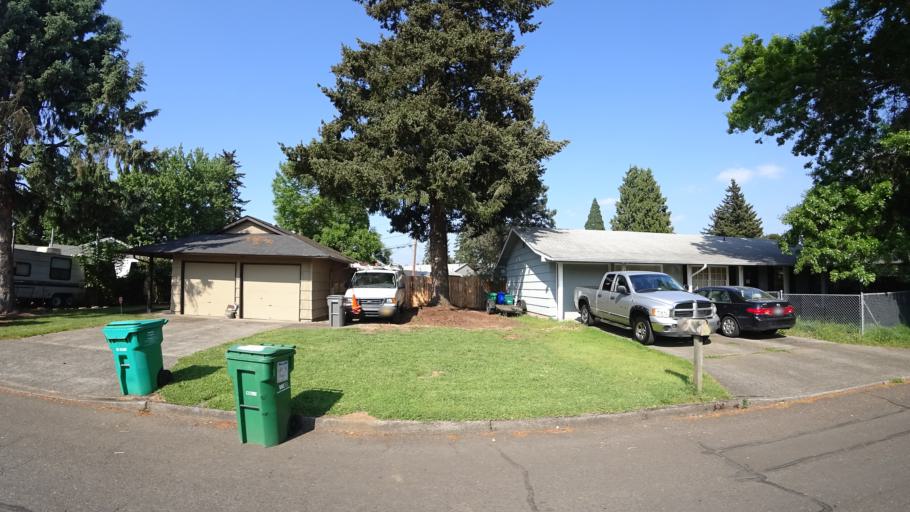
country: US
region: Oregon
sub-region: Clackamas County
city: Happy Valley
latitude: 45.5107
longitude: -122.5015
